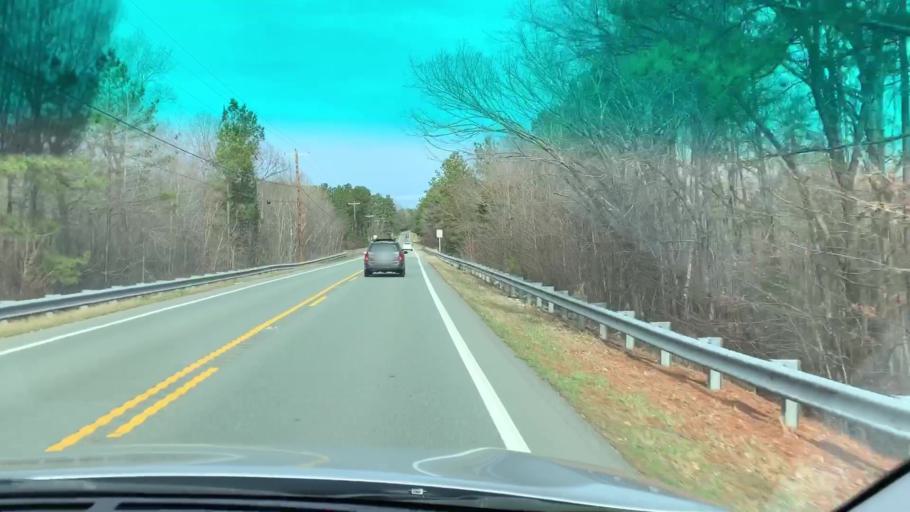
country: US
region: North Carolina
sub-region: Wake County
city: Green Level
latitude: 35.8545
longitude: -78.9393
